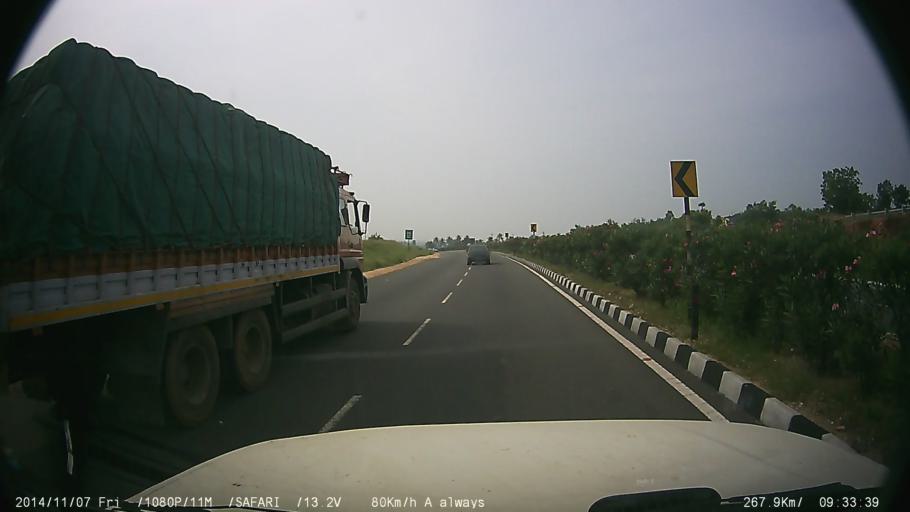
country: IN
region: Tamil Nadu
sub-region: Erode
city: Bhavani
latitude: 11.3978
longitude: 77.6519
